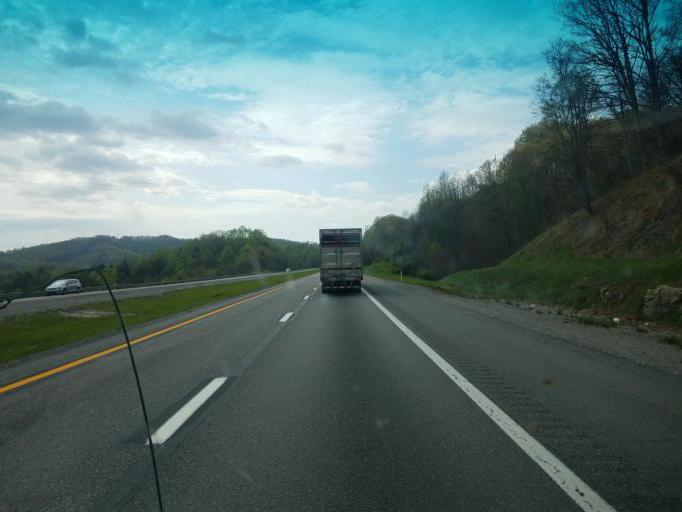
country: US
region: West Virginia
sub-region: Fayette County
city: Oak Hill
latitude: 37.9566
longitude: -81.2587
